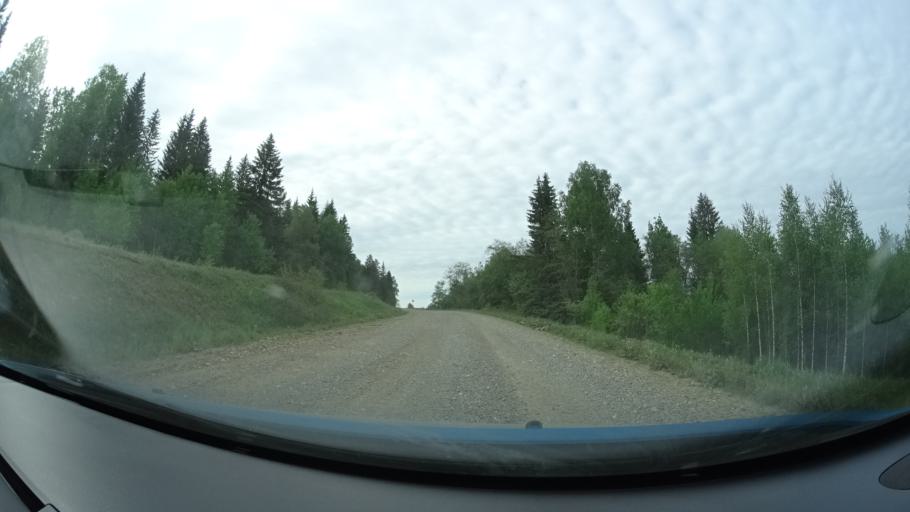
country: RU
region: Perm
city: Kuyeda
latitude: 56.6562
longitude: 55.6919
